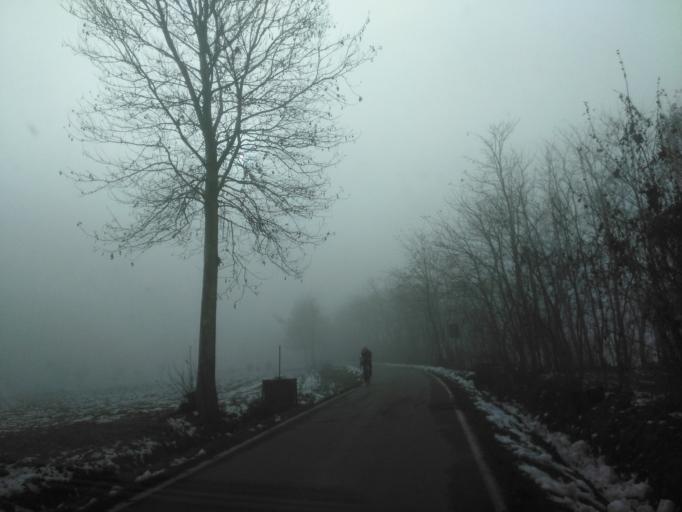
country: IT
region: Lombardy
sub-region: Provincia di Brescia
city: Azzano Mella
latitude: 45.4397
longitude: 10.1308
